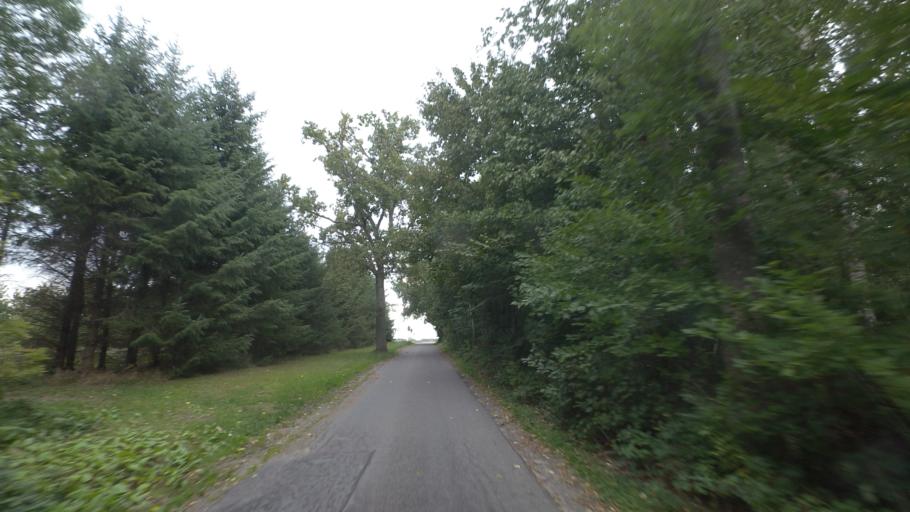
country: DK
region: Capital Region
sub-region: Bornholm Kommune
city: Nexo
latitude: 55.0024
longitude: 15.0377
